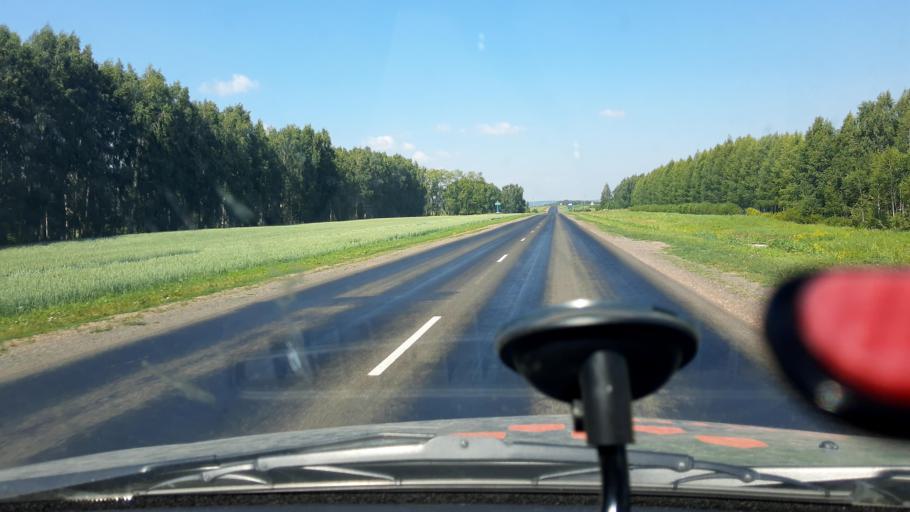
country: RU
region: Bashkortostan
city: Chekmagush
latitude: 55.0977
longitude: 54.6461
